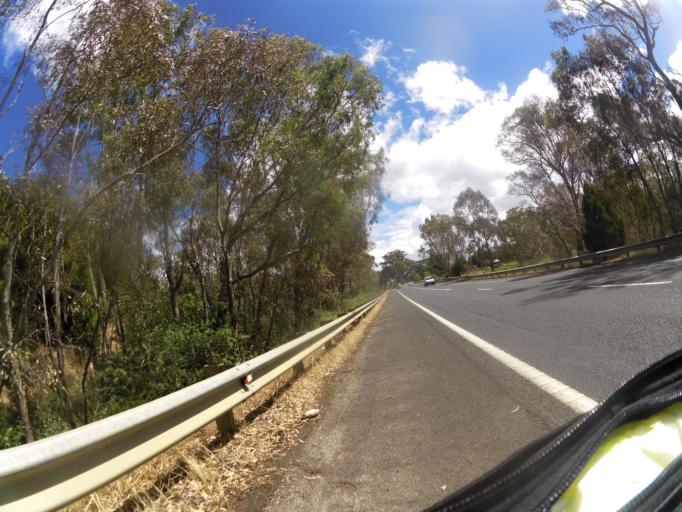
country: AU
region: Victoria
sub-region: Mount Alexander
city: Castlemaine
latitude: -37.0362
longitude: 144.2288
